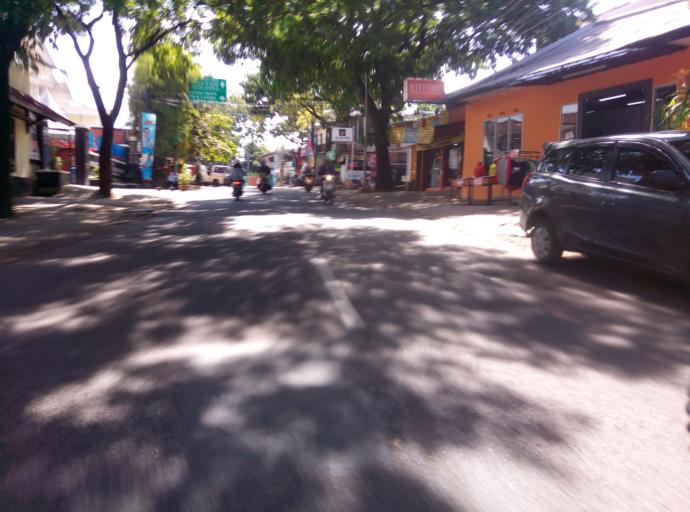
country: ID
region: West Java
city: Bandung
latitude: -6.8865
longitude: 107.6232
